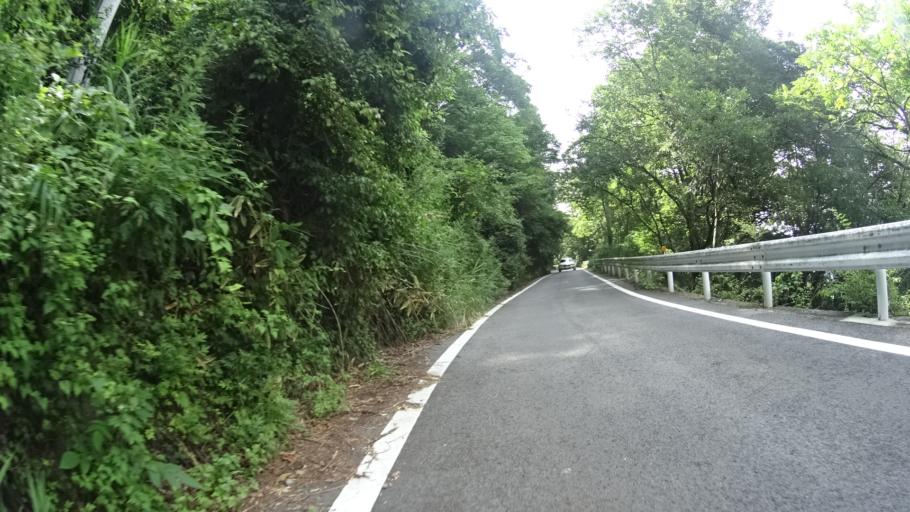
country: JP
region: Yamanashi
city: Nirasaki
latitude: 35.9100
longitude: 138.4238
